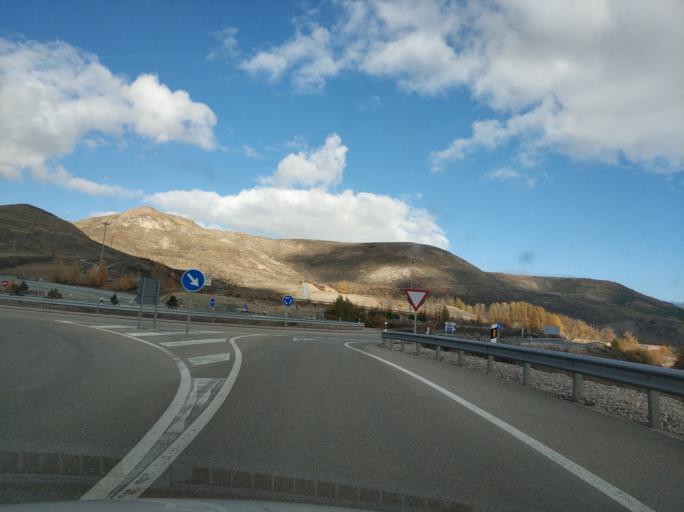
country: ES
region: Castille and Leon
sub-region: Provincia de Soria
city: Medinaceli
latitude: 41.1708
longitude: -2.4189
